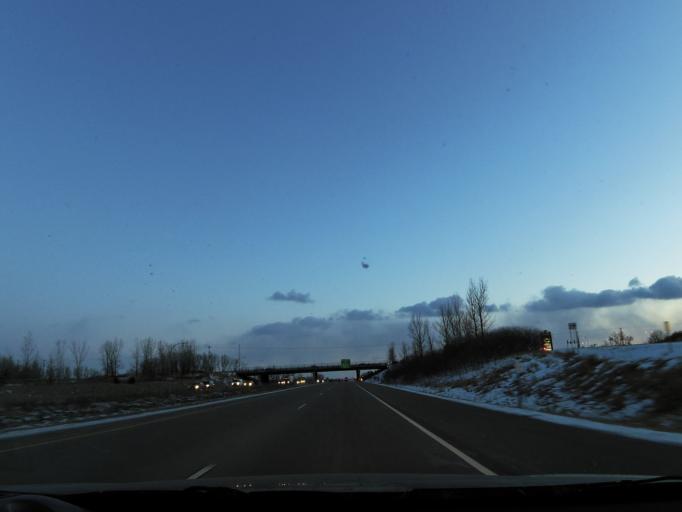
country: US
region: Minnesota
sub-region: Washington County
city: Oakdale
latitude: 44.9655
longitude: -92.9585
